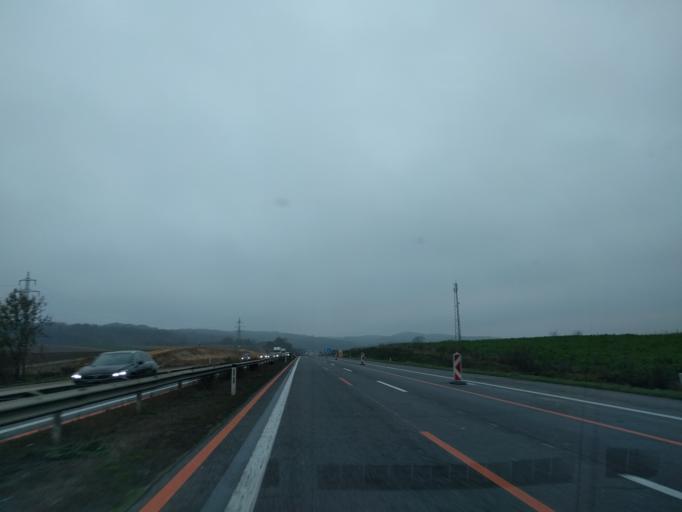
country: AT
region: Lower Austria
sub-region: Politischer Bezirk Melk
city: Leiben
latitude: 48.2031
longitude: 15.2643
